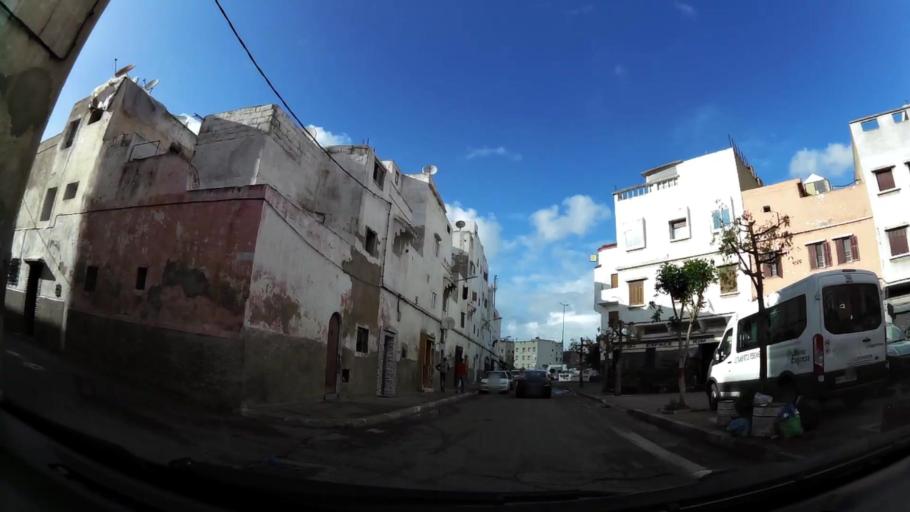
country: MA
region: Grand Casablanca
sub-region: Casablanca
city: Casablanca
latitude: 33.5532
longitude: -7.5923
